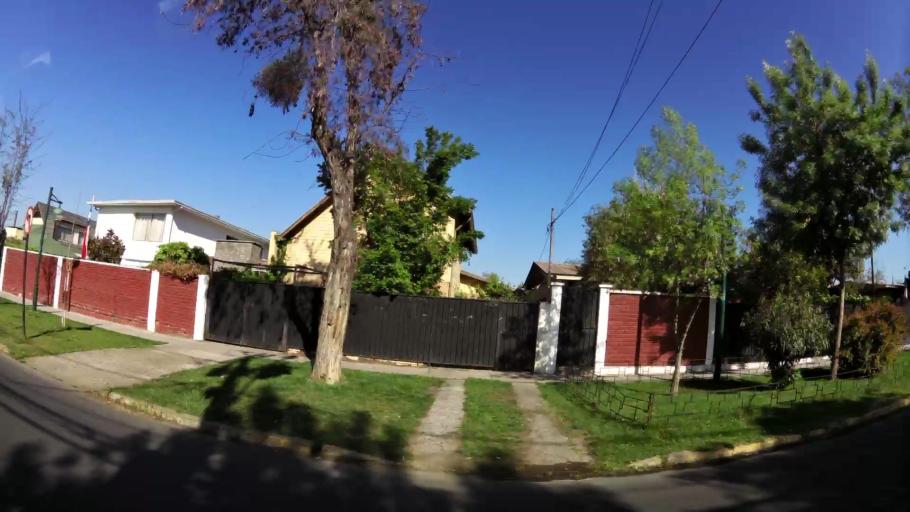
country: CL
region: Santiago Metropolitan
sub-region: Provincia de Santiago
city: Villa Presidente Frei, Nunoa, Santiago, Chile
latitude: -33.4429
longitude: -70.5815
